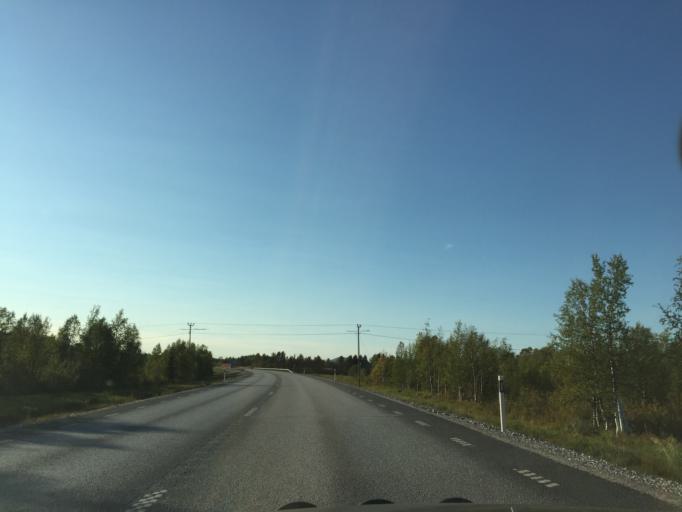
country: SE
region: Norrbotten
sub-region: Gallivare Kommun
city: Malmberget
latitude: 67.6433
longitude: 21.0527
